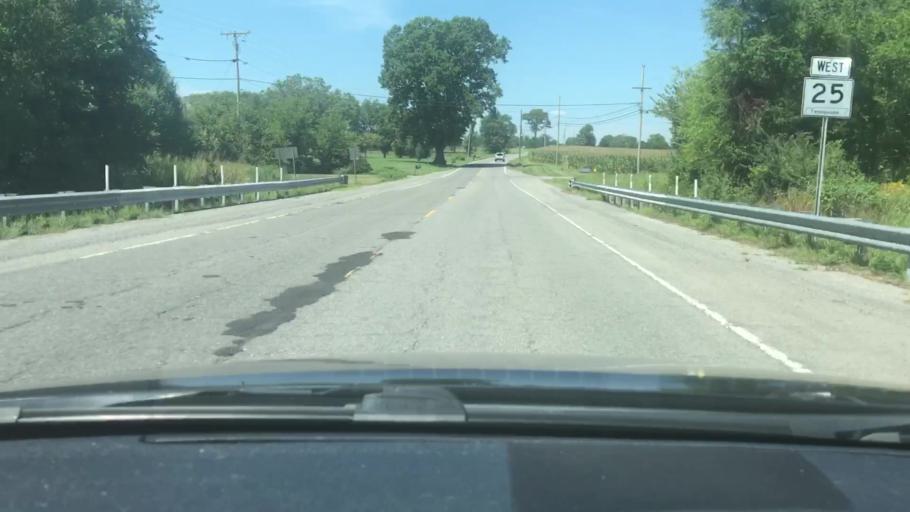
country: US
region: Tennessee
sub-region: Sumner County
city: Gallatin
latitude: 36.4013
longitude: -86.4878
